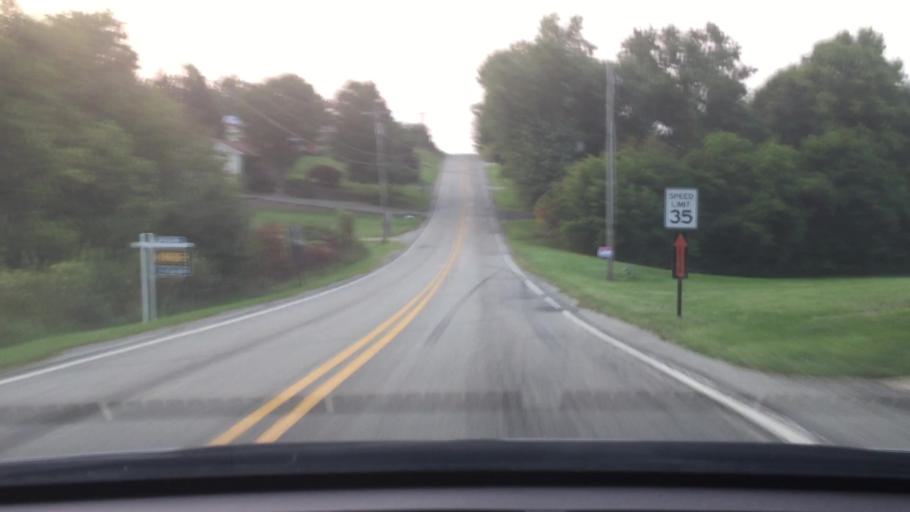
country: US
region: Pennsylvania
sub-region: Westmoreland County
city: Fellsburg
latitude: 40.1768
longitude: -79.8214
